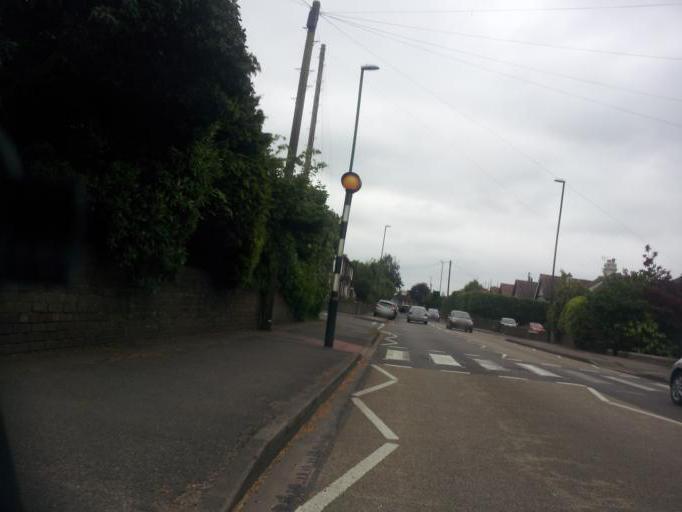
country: GB
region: England
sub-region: Kent
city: Maidstone
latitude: 51.2463
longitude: 0.5246
